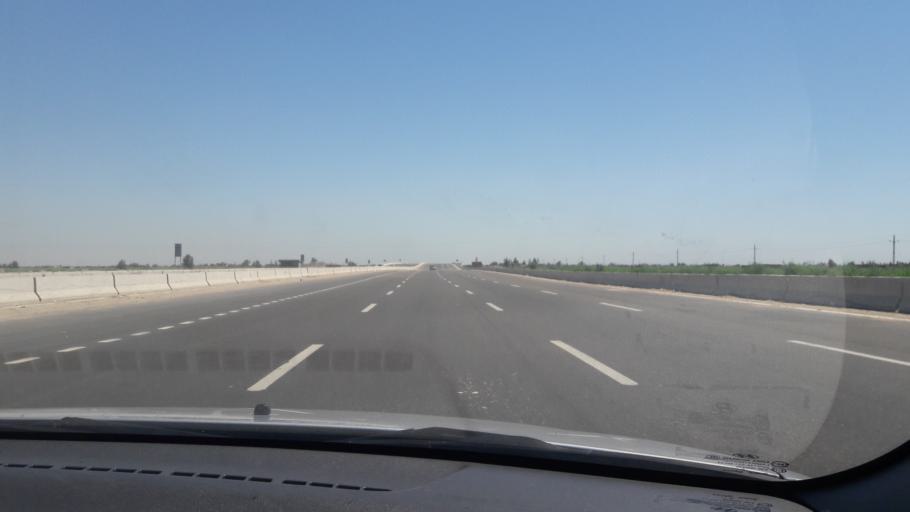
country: EG
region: Muhafazat Bur Sa`id
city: Port Said
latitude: 31.1801
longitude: 32.2351
